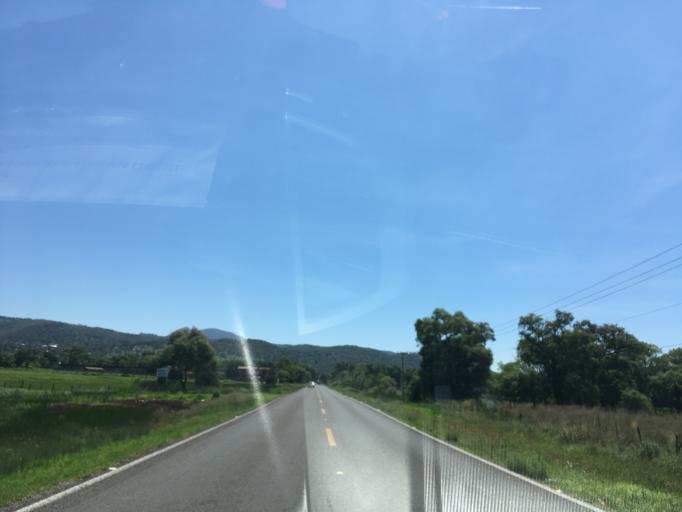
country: MX
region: Michoacan
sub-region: Hidalgo
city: Colonia Ecologica Asociacion de Lucha Social (Lucha Social)
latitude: 19.6939
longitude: -100.6163
